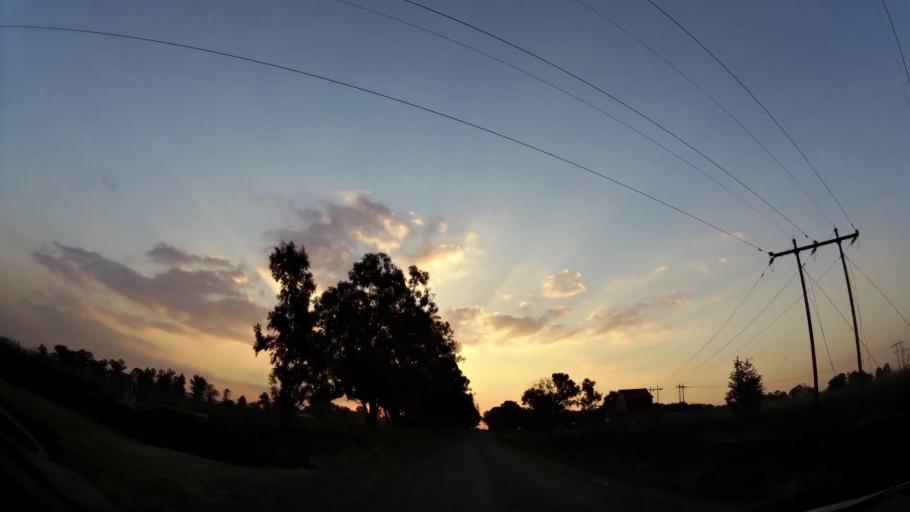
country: ZA
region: Gauteng
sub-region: Ekurhuleni Metropolitan Municipality
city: Springs
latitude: -26.3323
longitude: 28.4342
